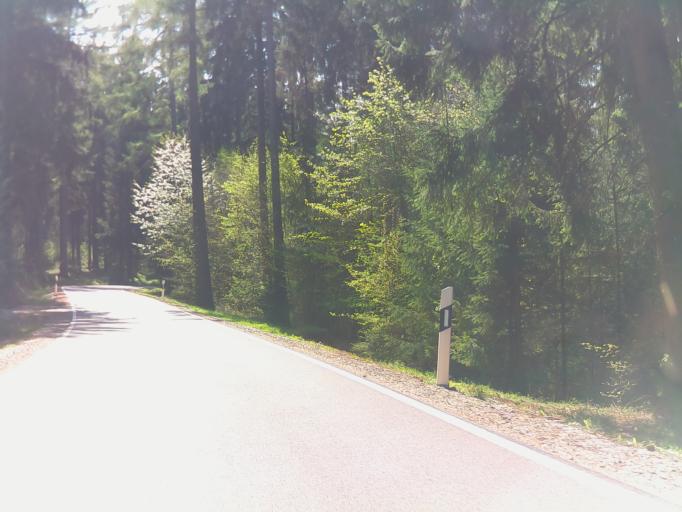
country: DE
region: Thuringia
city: Hildburghausen
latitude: 50.4518
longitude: 10.7736
